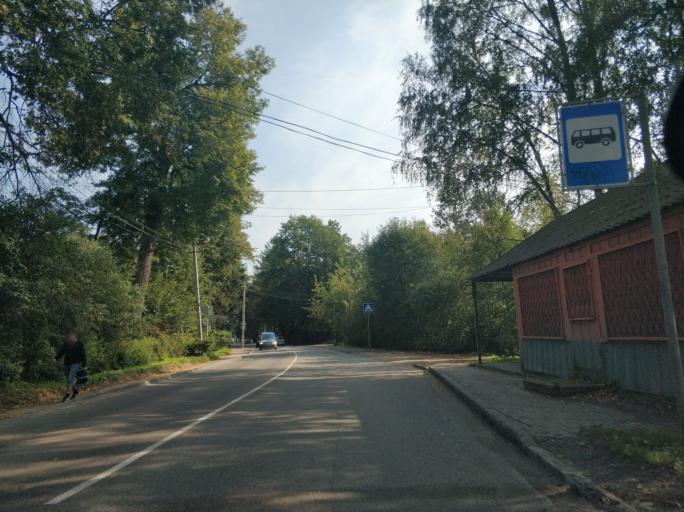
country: RU
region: Leningrad
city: Vsevolozhsk
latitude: 60.0087
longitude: 30.6013
